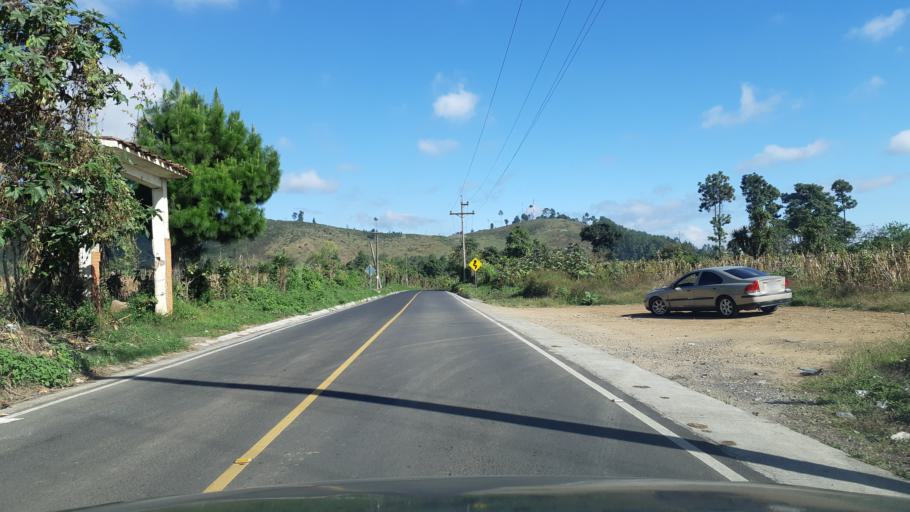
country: GT
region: Chimaltenango
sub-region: Municipio de Chimaltenango
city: Chimaltenango
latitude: 14.6395
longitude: -90.8245
